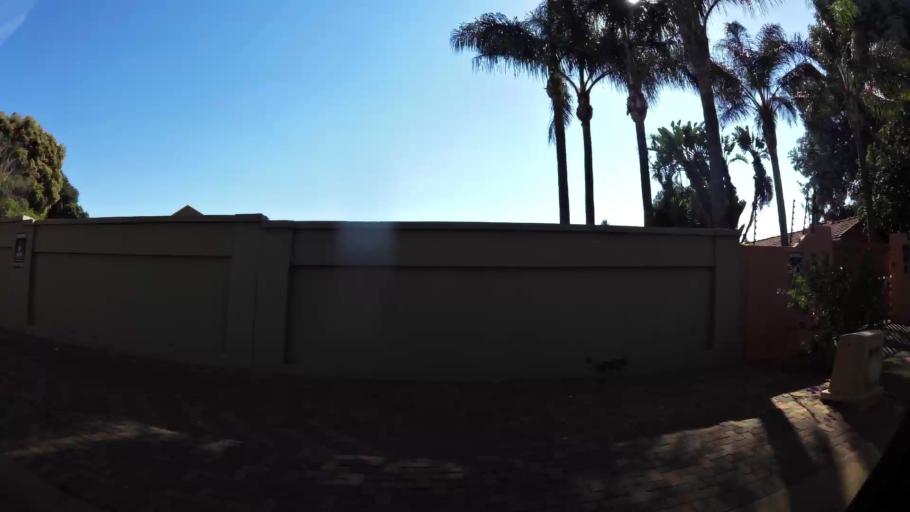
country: ZA
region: Gauteng
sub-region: City of Johannesburg Metropolitan Municipality
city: Roodepoort
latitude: -26.1194
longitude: 27.9217
